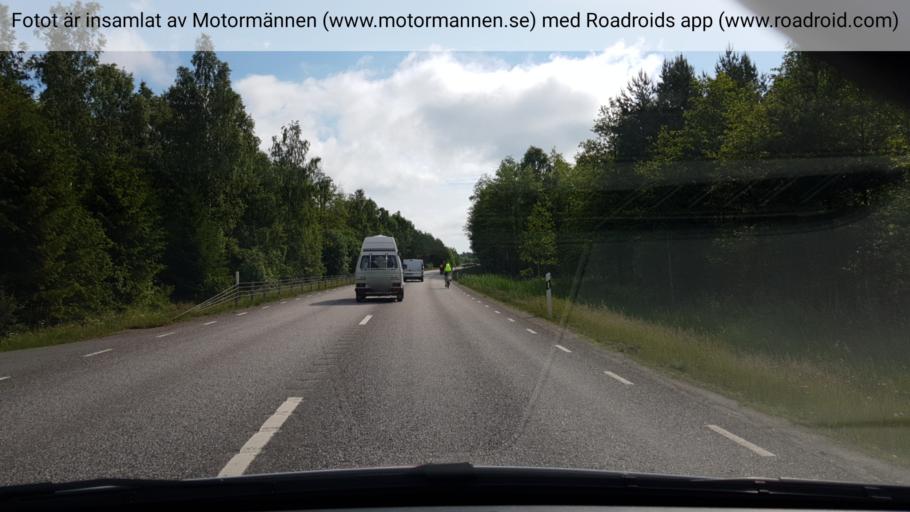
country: SE
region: Vaestra Goetaland
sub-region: Karlsborgs Kommun
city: Karlsborg
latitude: 58.5170
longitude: 14.4906
